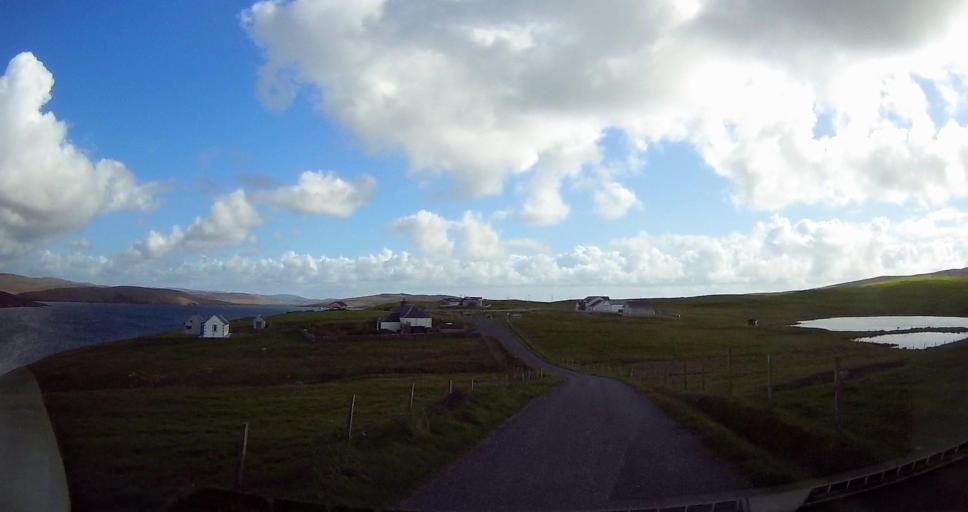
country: GB
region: Scotland
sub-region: Shetland Islands
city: Lerwick
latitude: 60.3663
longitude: -1.3819
